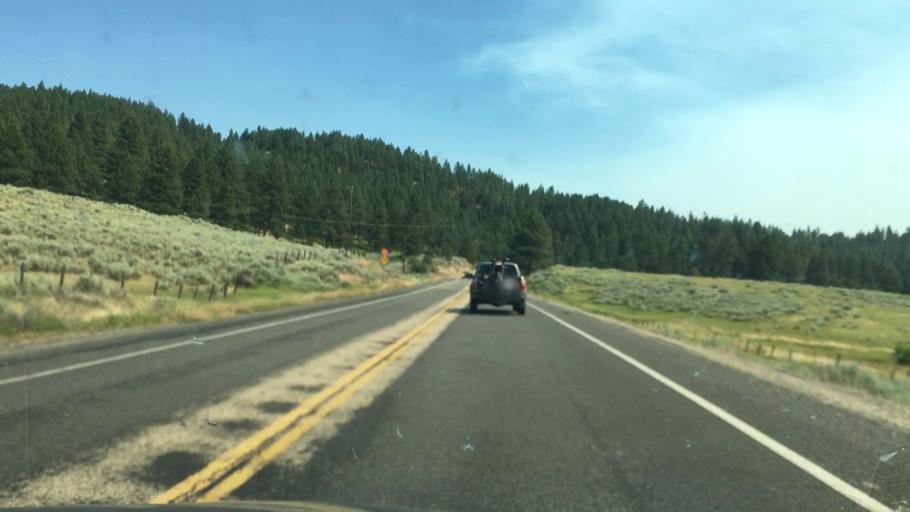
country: US
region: Idaho
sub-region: Valley County
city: Cascade
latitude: 44.5967
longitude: -116.0456
